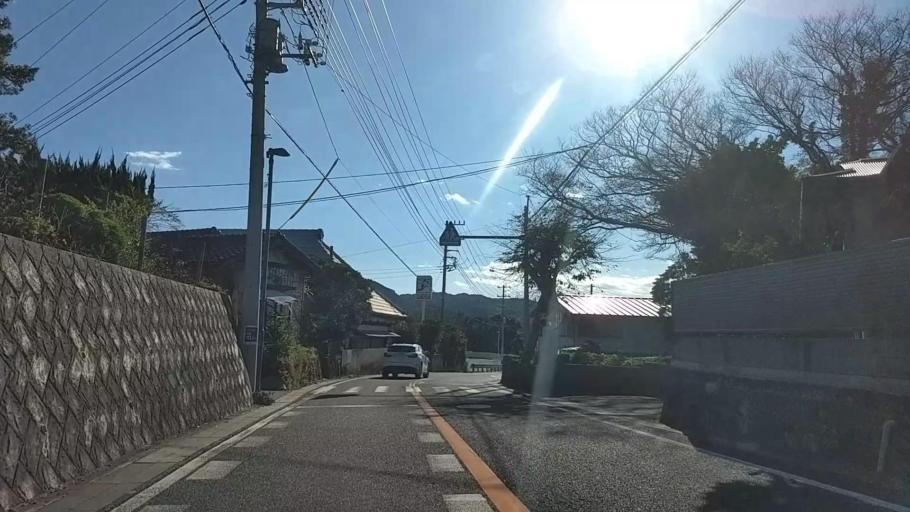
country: JP
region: Chiba
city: Futtsu
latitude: 35.1471
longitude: 139.8324
